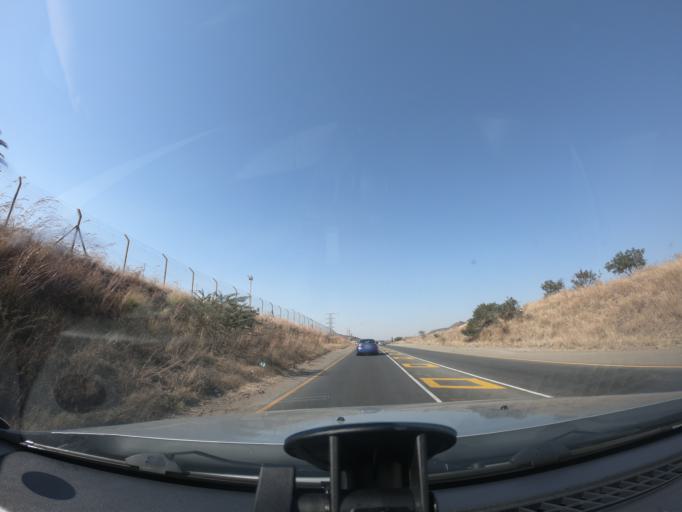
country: ZA
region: KwaZulu-Natal
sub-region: uThukela District Municipality
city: Ladysmith
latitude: -28.5500
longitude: 29.8304
